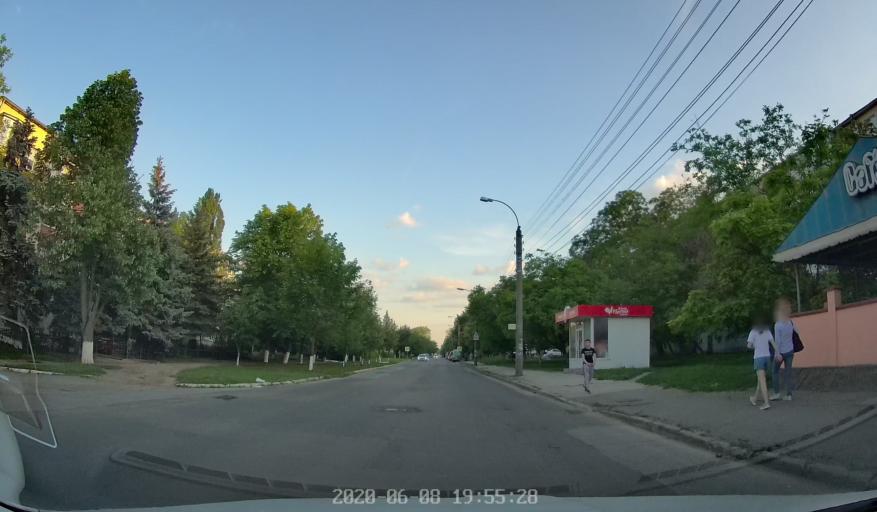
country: MD
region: Chisinau
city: Chisinau
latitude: 47.0286
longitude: 28.8838
